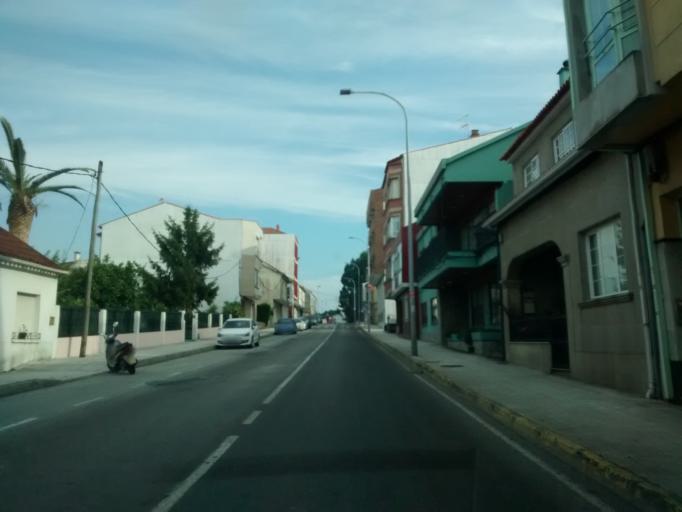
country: ES
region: Galicia
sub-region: Provincia de Pontevedra
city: O Grove
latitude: 42.4886
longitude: -8.8662
